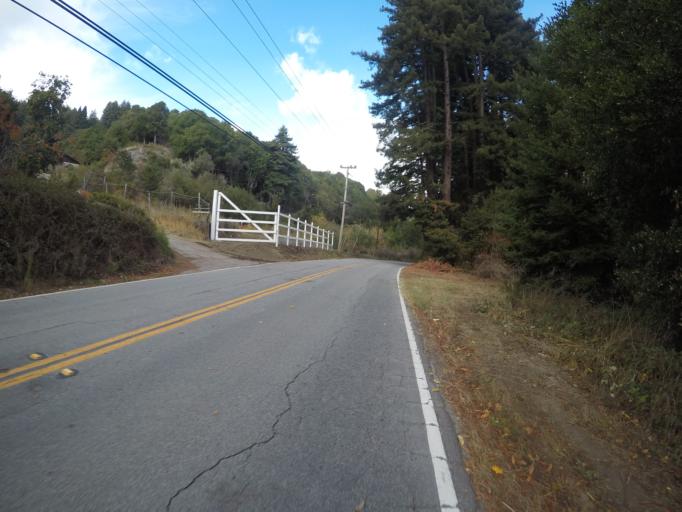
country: US
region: California
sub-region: Santa Cruz County
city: Scotts Valley
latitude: 37.0466
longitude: -121.9834
